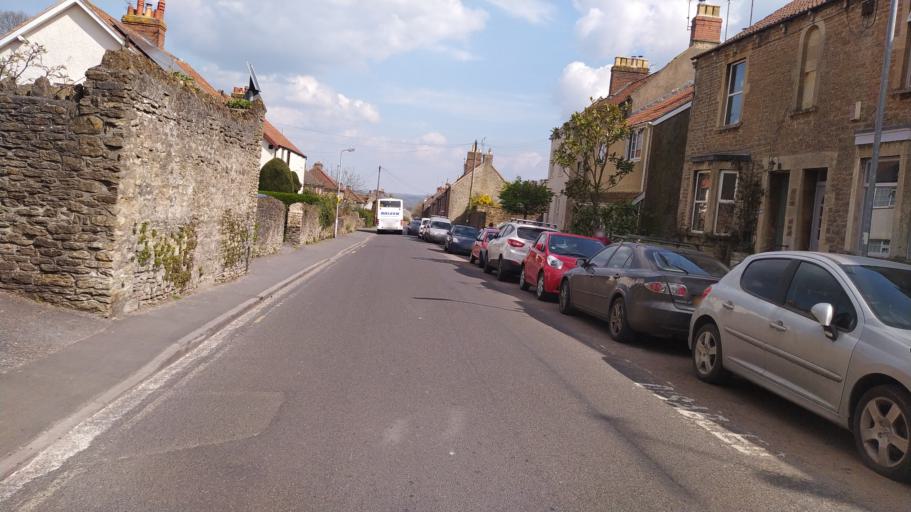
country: GB
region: England
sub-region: Somerset
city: Frome
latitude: 51.2322
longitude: -2.3356
